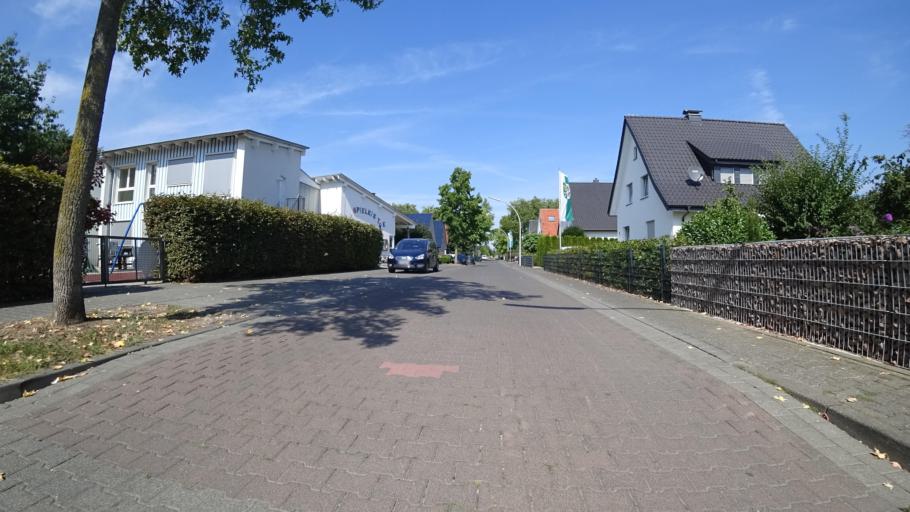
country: DE
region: North Rhine-Westphalia
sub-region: Regierungsbezirk Detmold
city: Rheda-Wiedenbruck
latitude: 51.8623
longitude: 8.2868
